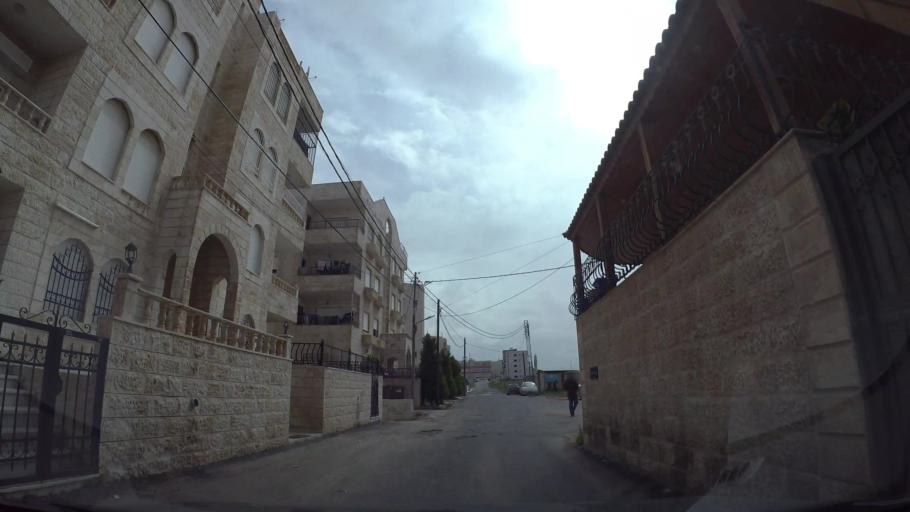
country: JO
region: Amman
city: Amman
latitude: 31.9969
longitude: 35.9340
